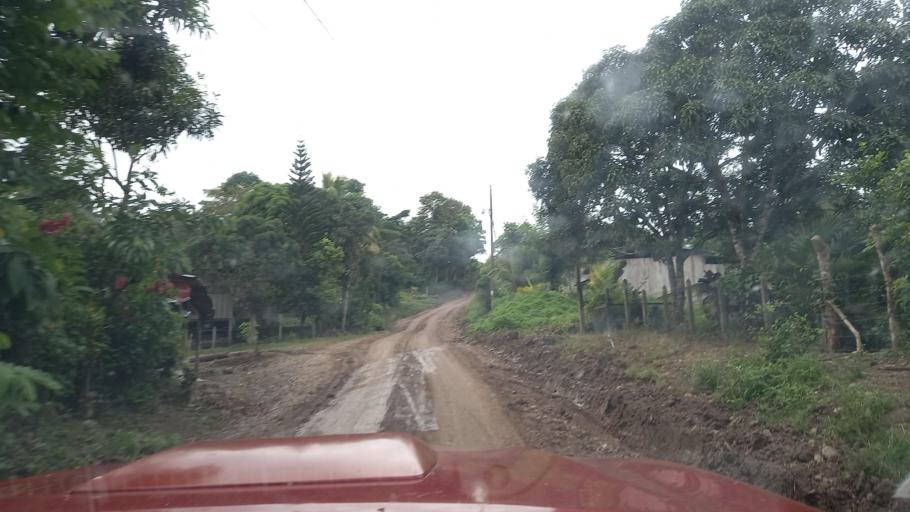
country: NI
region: Jinotega
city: San Jose de Bocay
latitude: 13.3492
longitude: -85.6596
